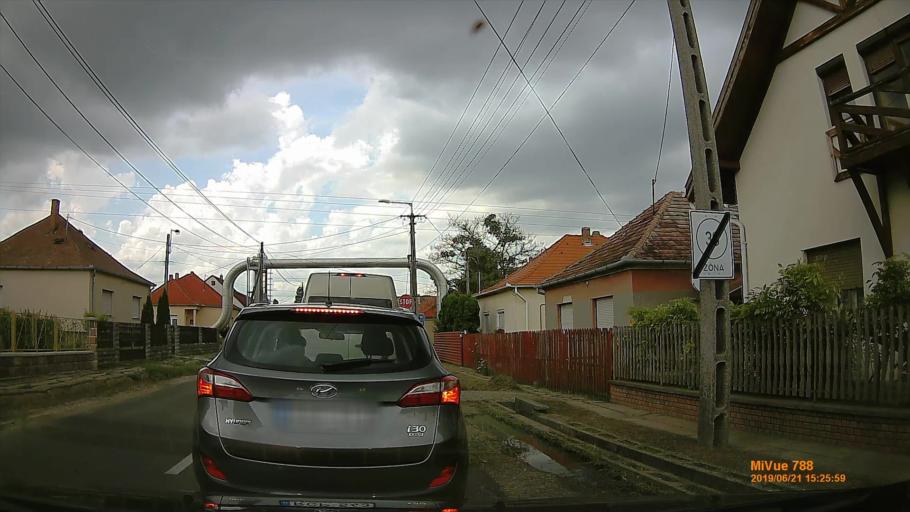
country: HU
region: Baranya
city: Pecs
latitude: 46.0454
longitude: 18.2478
